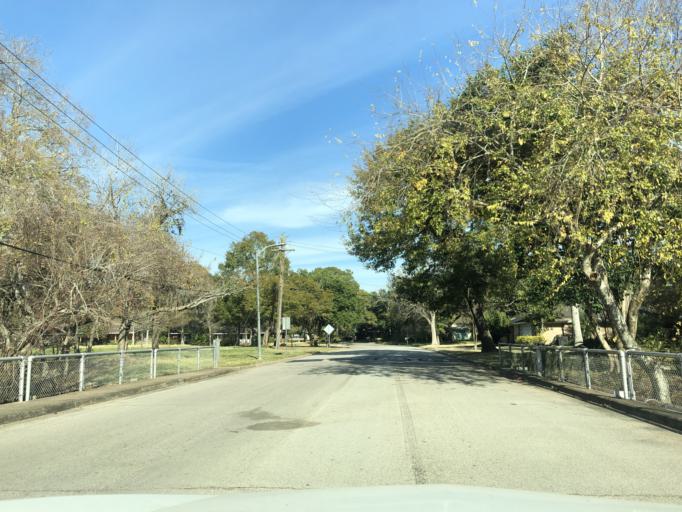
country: US
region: Texas
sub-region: Fort Bend County
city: Missouri City
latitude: 29.6760
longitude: -95.5153
